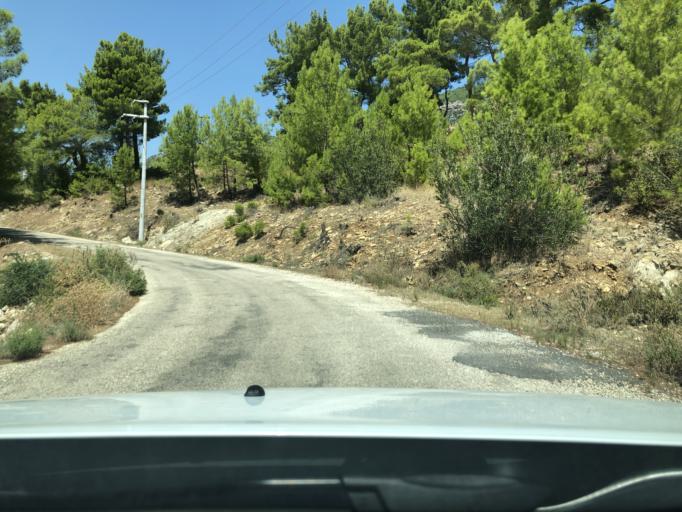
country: TR
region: Antalya
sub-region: Manavgat
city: Manavgat
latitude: 36.8806
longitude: 31.5503
